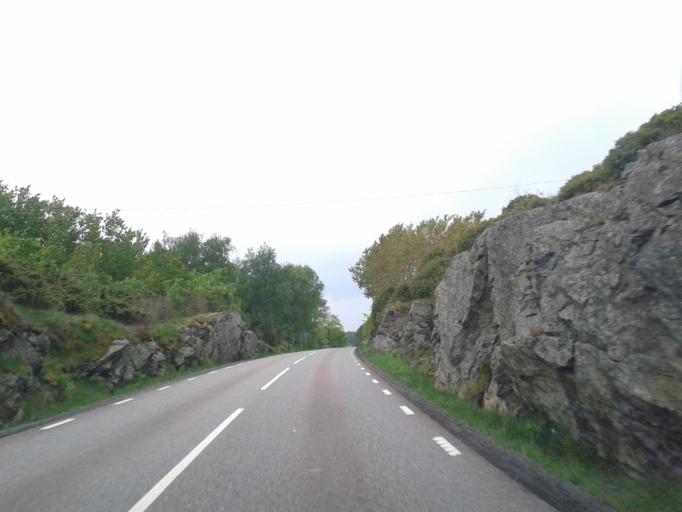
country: SE
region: Vaestra Goetaland
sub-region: Kungalvs Kommun
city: Marstrand
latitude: 57.8947
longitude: 11.7146
